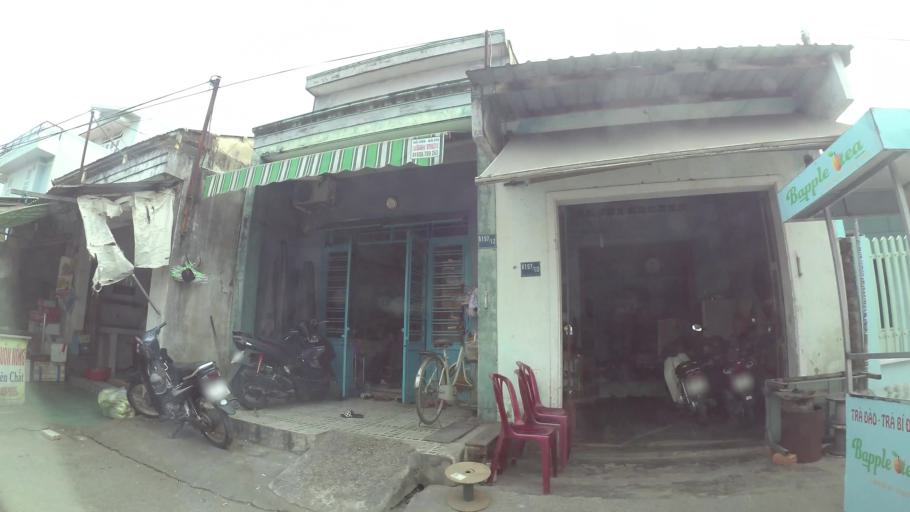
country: VN
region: Da Nang
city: Son Tra
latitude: 16.0920
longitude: 108.2441
